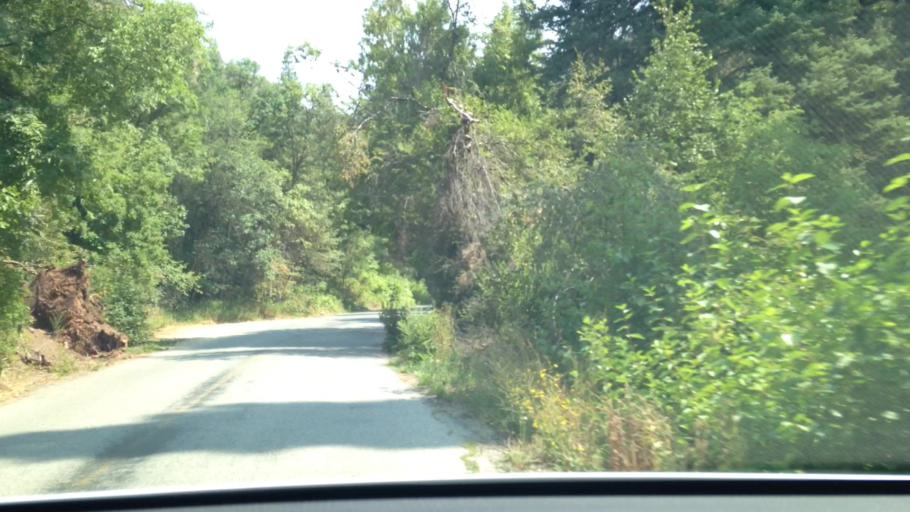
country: US
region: Utah
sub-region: Salt Lake County
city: Mount Olympus
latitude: 40.7023
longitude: -111.6973
